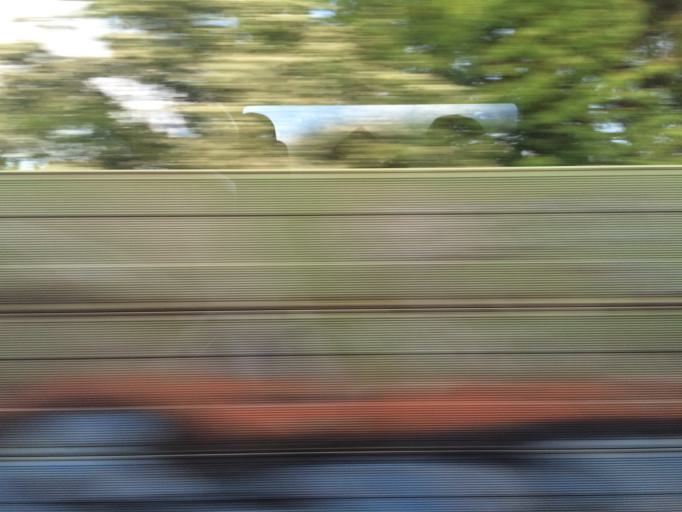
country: DE
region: North Rhine-Westphalia
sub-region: Regierungsbezirk Dusseldorf
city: Langenfeld
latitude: 51.0709
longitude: 6.9577
